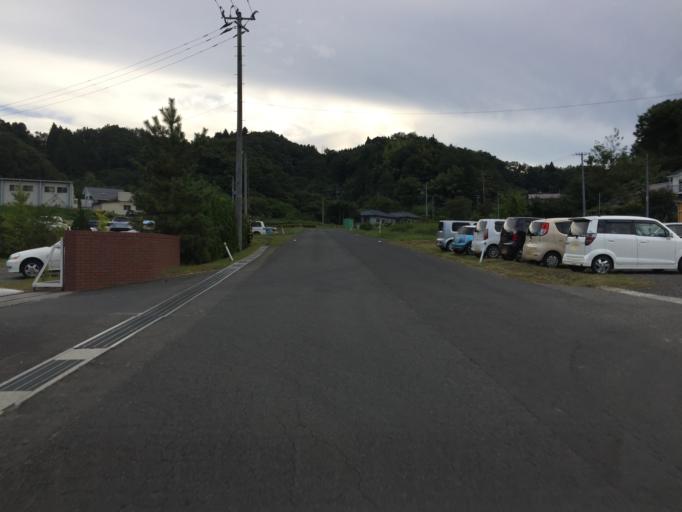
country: JP
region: Fukushima
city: Fukushima-shi
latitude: 37.6771
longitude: 140.5785
